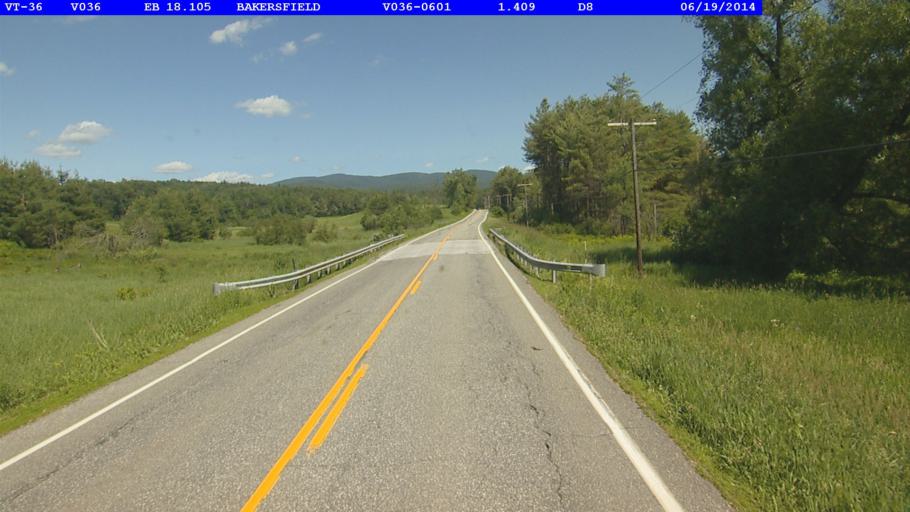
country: US
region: Vermont
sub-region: Franklin County
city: Enosburg Falls
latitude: 44.7816
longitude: -72.8227
